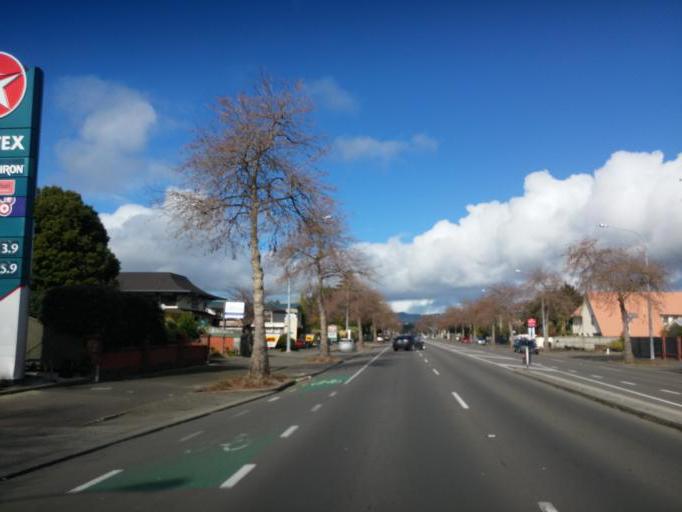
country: NZ
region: Manawatu-Wanganui
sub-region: Palmerston North City
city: Palmerston North
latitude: -40.3626
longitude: 175.6162
